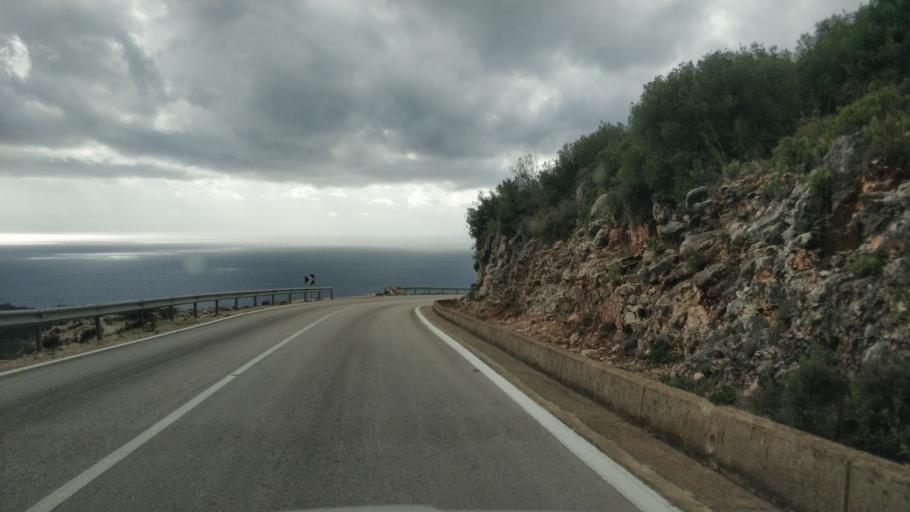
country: AL
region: Vlore
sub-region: Rrethi i Vlores
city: Vranisht
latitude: 40.1418
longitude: 19.6633
